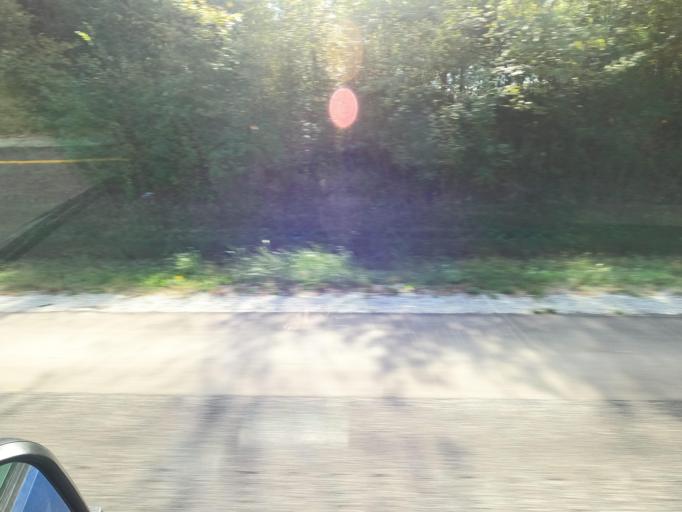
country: US
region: Tennessee
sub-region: Crockett County
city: Bells
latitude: 35.6138
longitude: -89.0102
